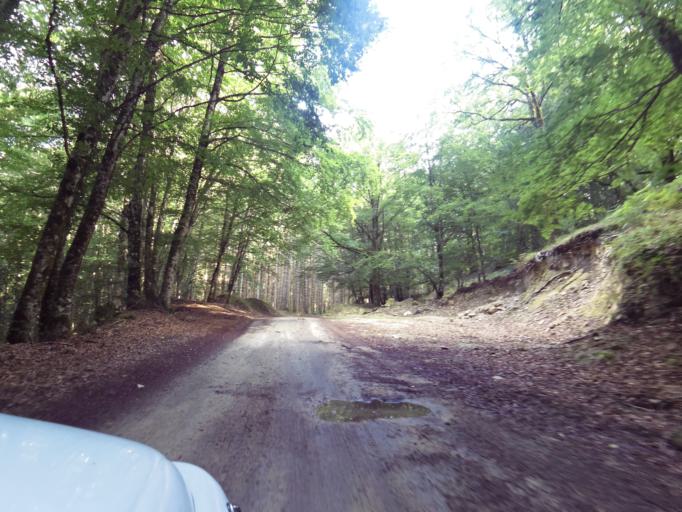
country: IT
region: Calabria
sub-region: Provincia di Vibo-Valentia
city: Nardodipace
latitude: 38.5118
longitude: 16.3795
